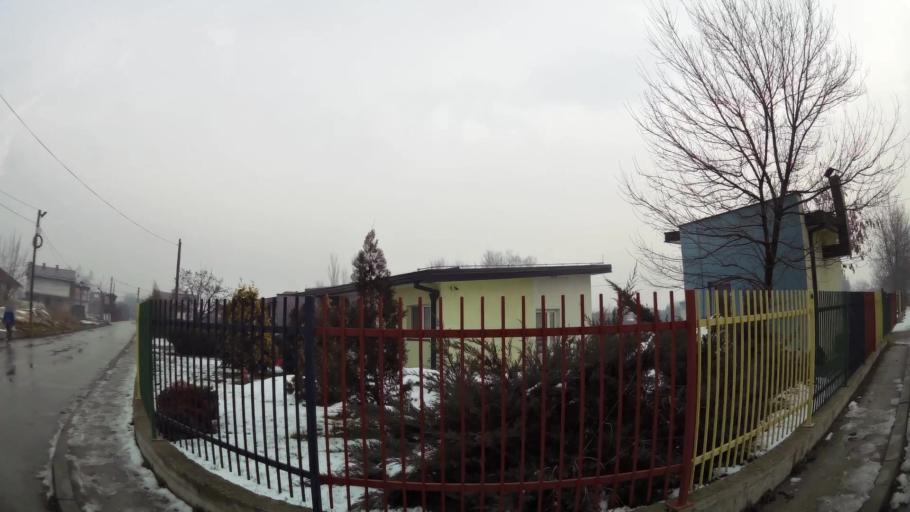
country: MK
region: Ilinden
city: Jurumleri
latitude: 41.9641
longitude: 21.5597
